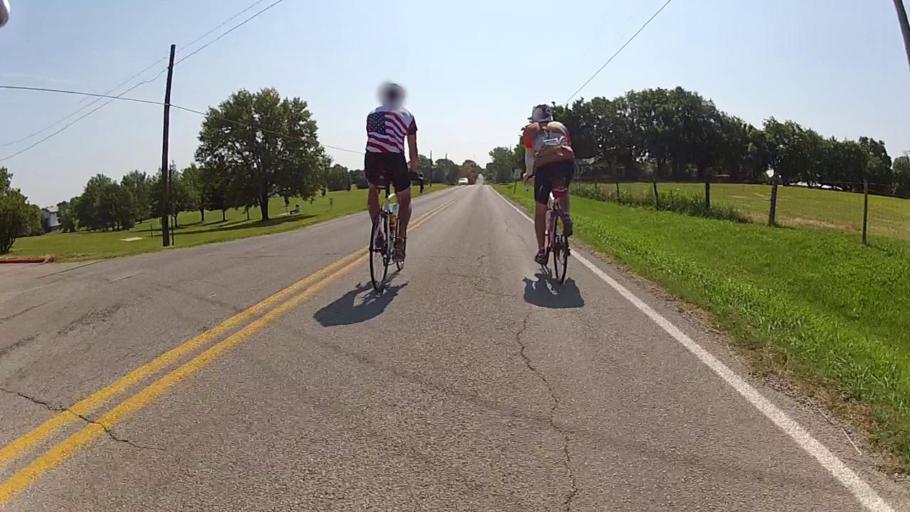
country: US
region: Kansas
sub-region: Montgomery County
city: Independence
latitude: 37.1929
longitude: -95.7205
